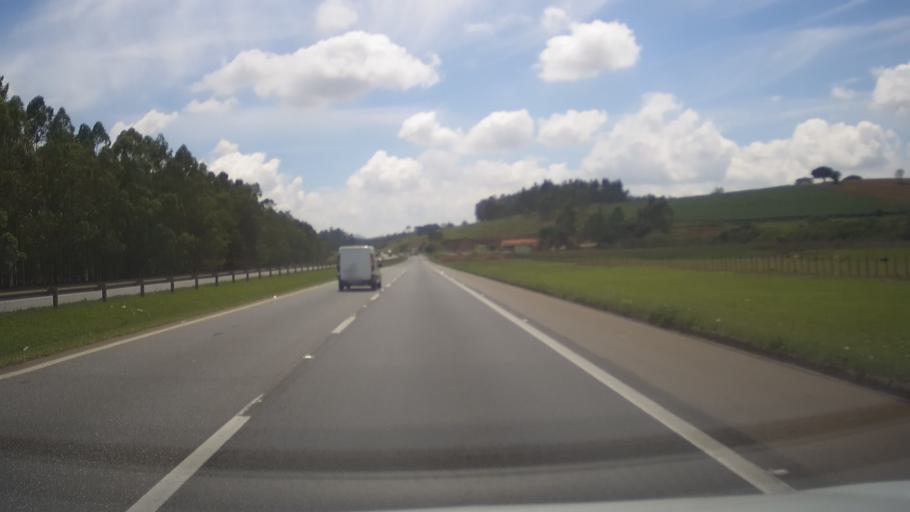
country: BR
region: Minas Gerais
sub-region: Santa Rita Do Sapucai
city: Santa Rita do Sapucai
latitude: -22.0962
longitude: -45.7149
